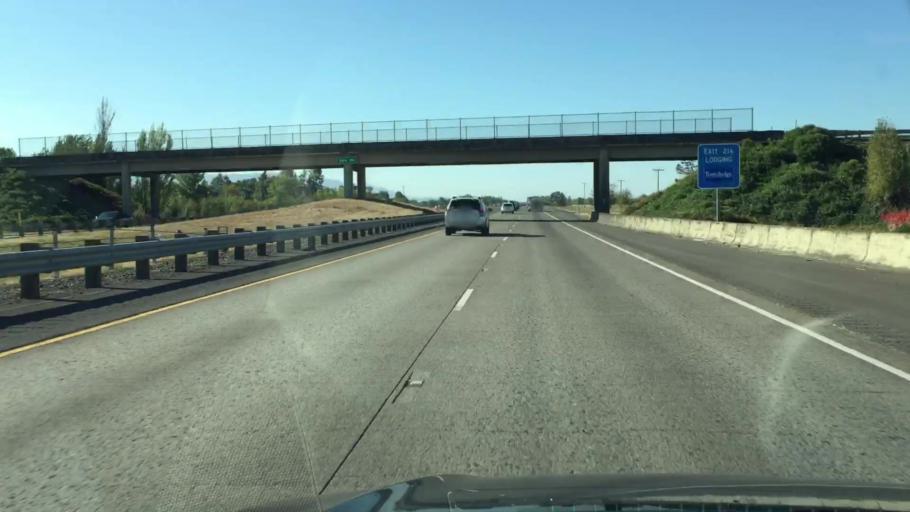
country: US
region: Oregon
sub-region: Linn County
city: Brownsville
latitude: 44.4138
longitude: -123.0622
